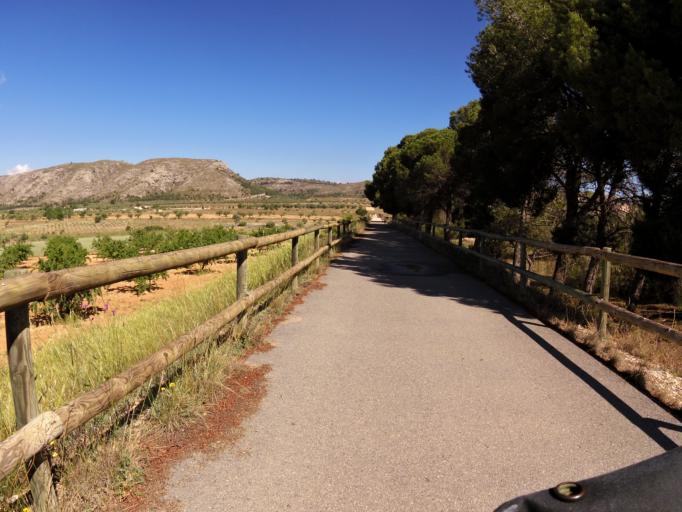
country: ES
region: Valencia
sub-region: Provincia de Alicante
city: Canada
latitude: 38.6412
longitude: -0.8100
